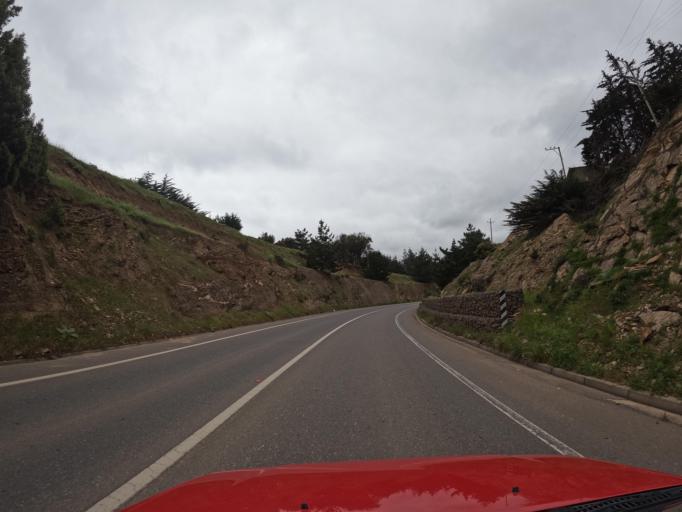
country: CL
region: O'Higgins
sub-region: Provincia de Colchagua
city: Santa Cruz
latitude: -34.4834
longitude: -72.0192
